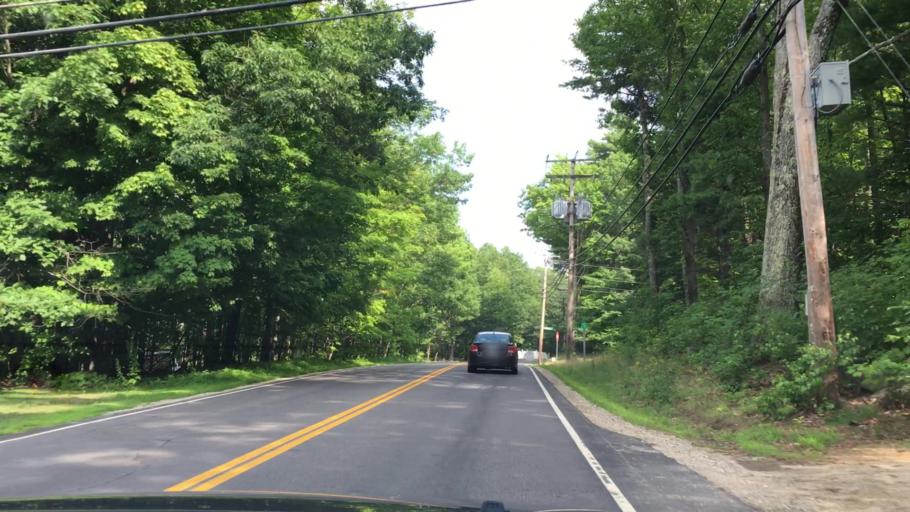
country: US
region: New Hampshire
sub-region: Belknap County
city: Gilford
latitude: 43.5688
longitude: -71.3435
